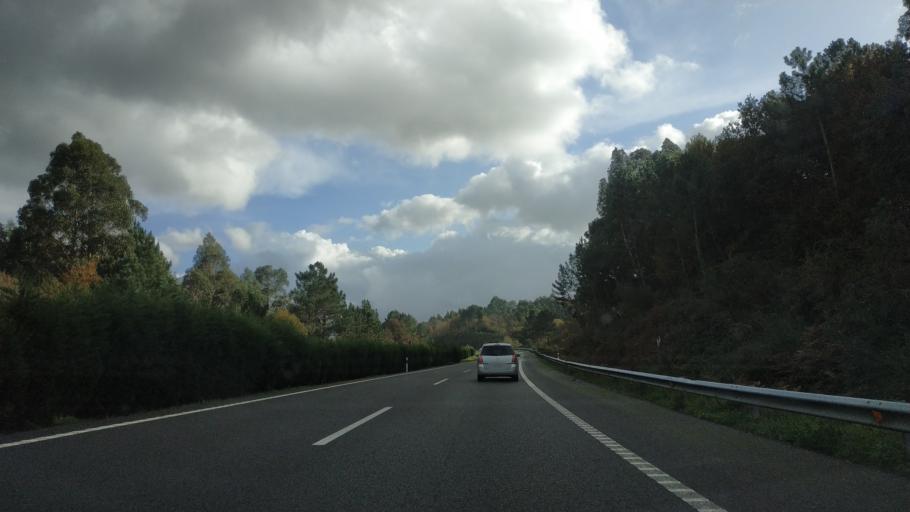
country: ES
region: Galicia
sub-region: Provincia da Coruna
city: Cambre
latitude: 43.2675
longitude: -8.3563
